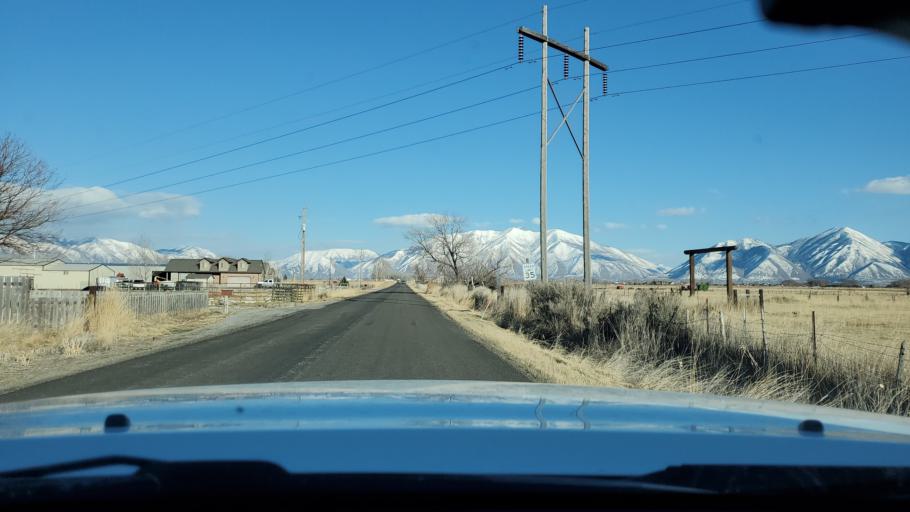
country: US
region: Utah
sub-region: Utah County
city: Benjamin
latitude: 40.1141
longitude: -111.7670
